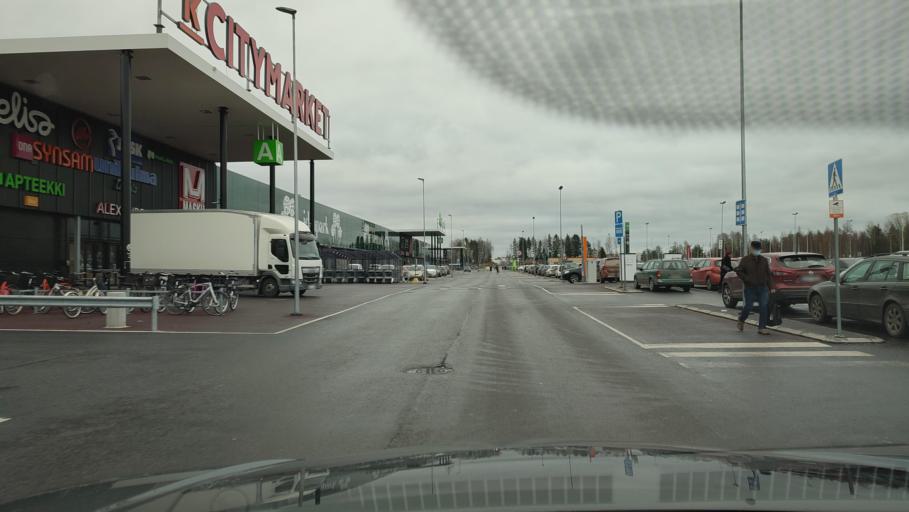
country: FI
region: Southern Ostrobothnia
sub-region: Seinaejoki
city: Seinaejoki
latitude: 62.7930
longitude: 22.7909
